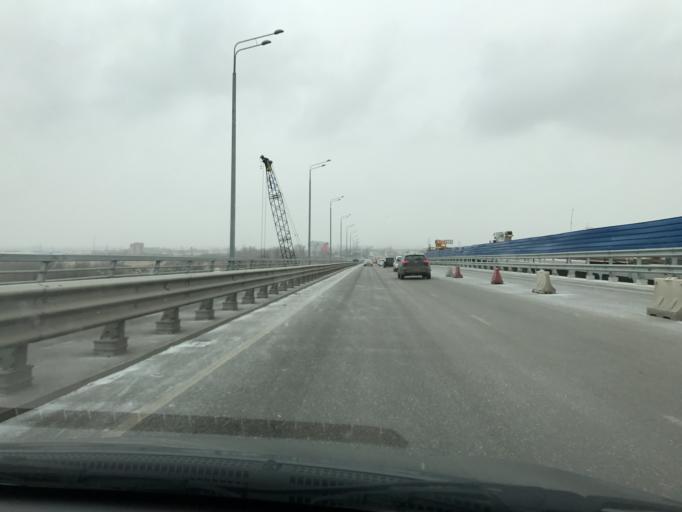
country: RU
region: Rostov
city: Rostov-na-Donu
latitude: 47.2143
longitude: 39.7226
